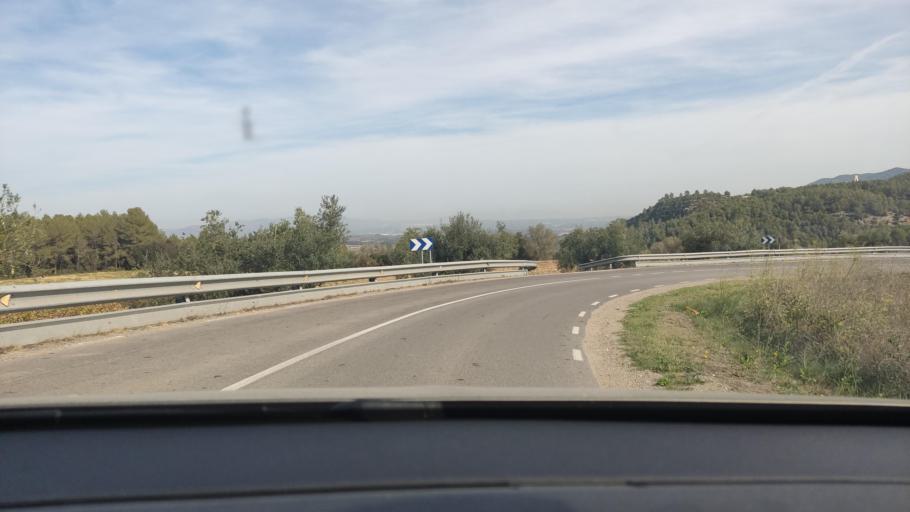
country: ES
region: Catalonia
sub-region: Provincia de Barcelona
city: Sant Sadurni d'Anoia
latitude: 41.4131
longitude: 1.8008
